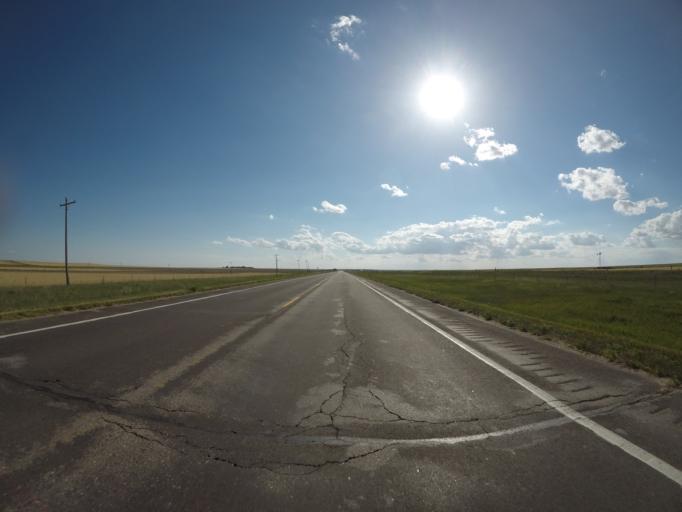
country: US
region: Colorado
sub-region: Morgan County
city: Fort Morgan
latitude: 40.6030
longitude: -103.8568
